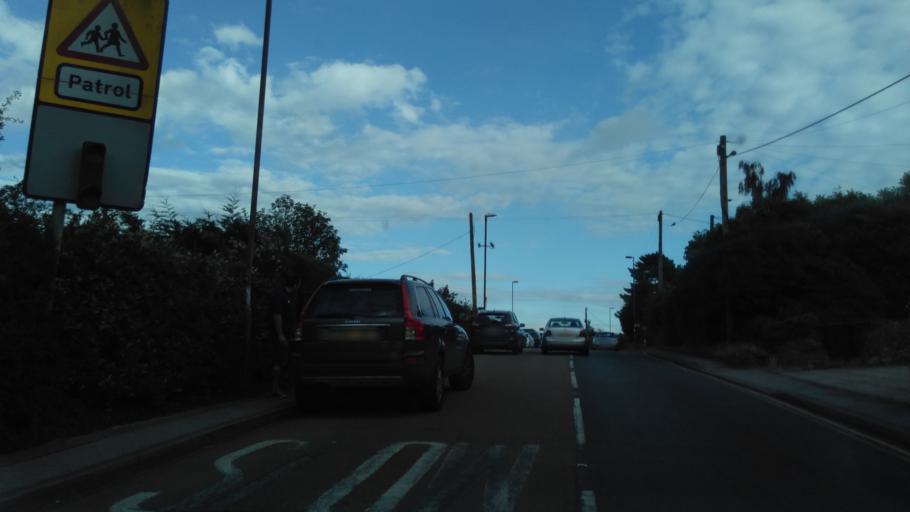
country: GB
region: England
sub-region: Kent
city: Blean
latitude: 51.2998
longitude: 1.0495
